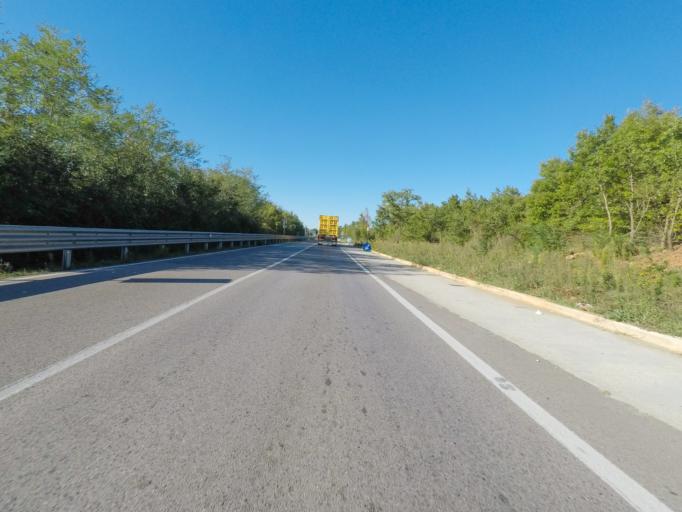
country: IT
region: Tuscany
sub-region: Provincia di Siena
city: Rosia
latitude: 43.2202
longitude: 11.2746
